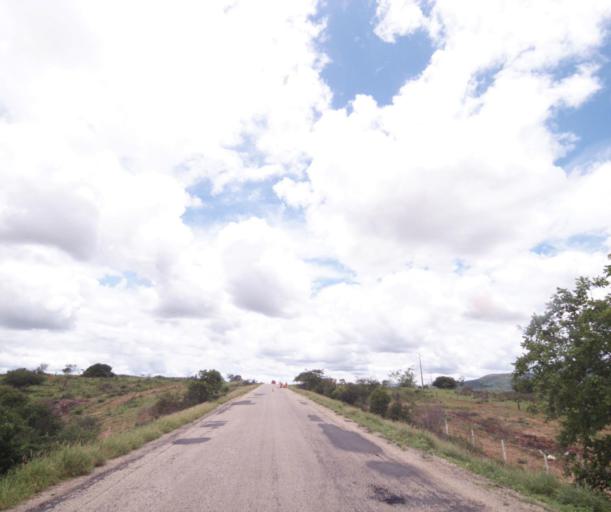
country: BR
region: Bahia
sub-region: Brumado
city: Brumado
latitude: -14.1576
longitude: -41.5222
